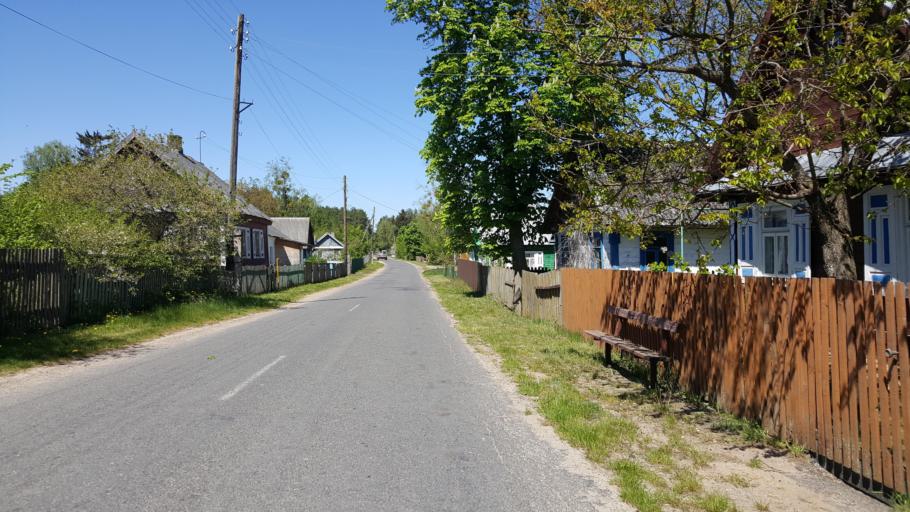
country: BY
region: Brest
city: Kamyanyuki
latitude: 52.5026
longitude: 23.7514
